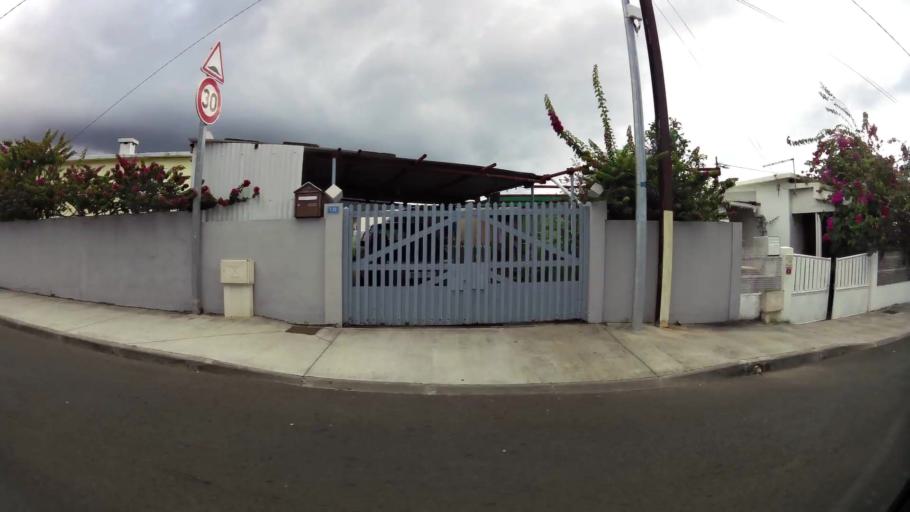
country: RE
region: Reunion
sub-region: Reunion
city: Saint-Denis
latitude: -20.8924
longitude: 55.4743
